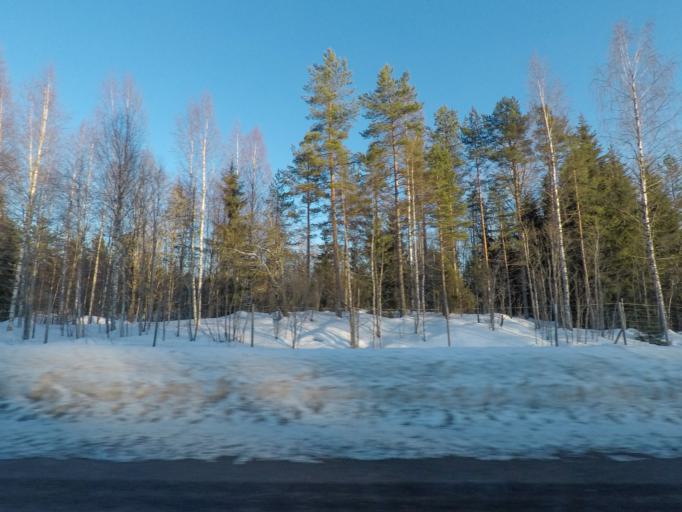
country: FI
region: Paijanne Tavastia
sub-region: Lahti
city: Heinola
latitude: 61.3521
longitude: 26.2214
